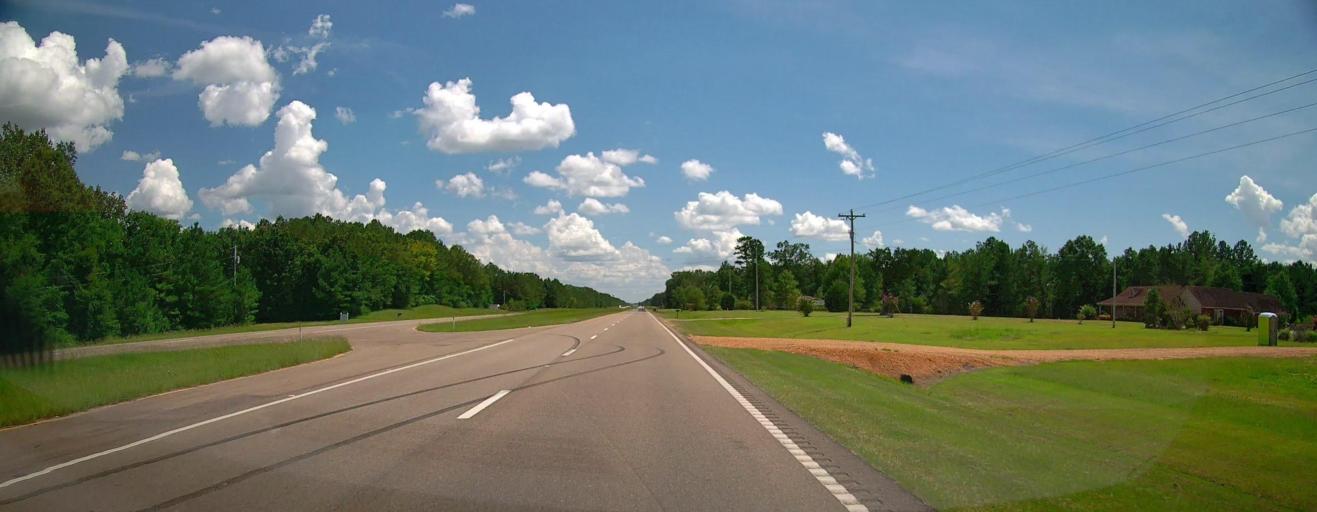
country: US
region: Mississippi
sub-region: Monroe County
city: Aberdeen
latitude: 33.9253
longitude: -88.5962
